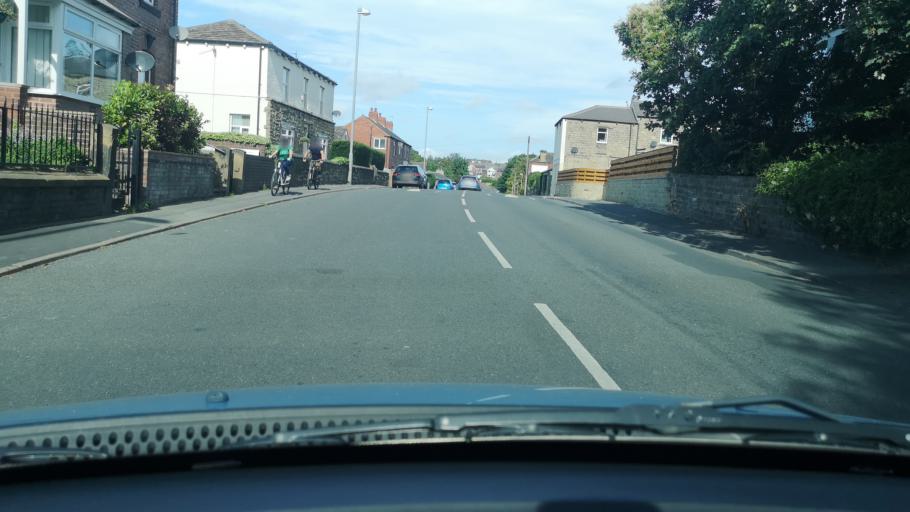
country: GB
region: England
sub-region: City and Borough of Wakefield
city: Ossett
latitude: 53.6730
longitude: -1.5769
